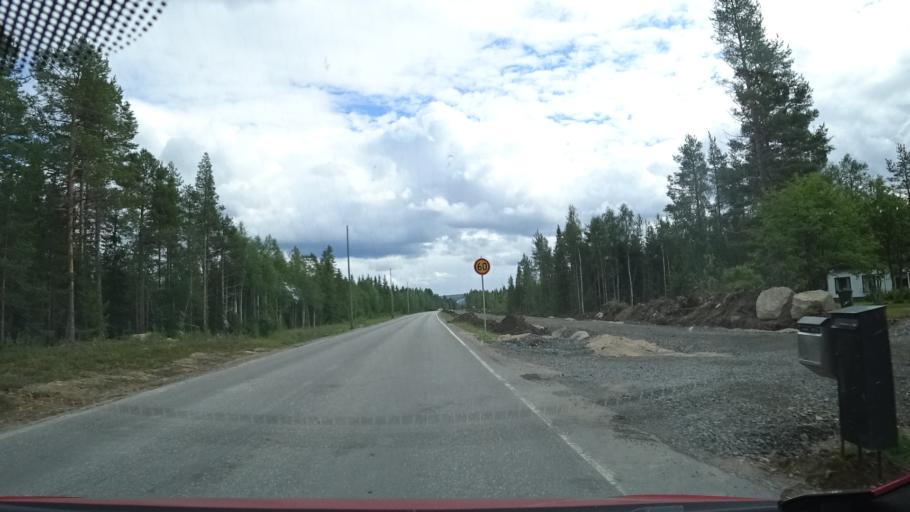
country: FI
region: Lapland
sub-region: Rovaniemi
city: Rovaniemi
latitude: 66.5366
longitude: 25.7264
